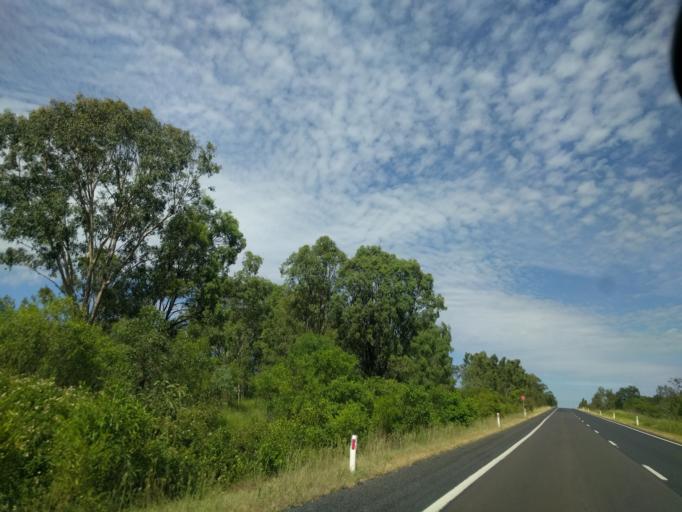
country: AU
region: Queensland
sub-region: Lockyer Valley
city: Gatton
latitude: -27.5365
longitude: 152.2674
